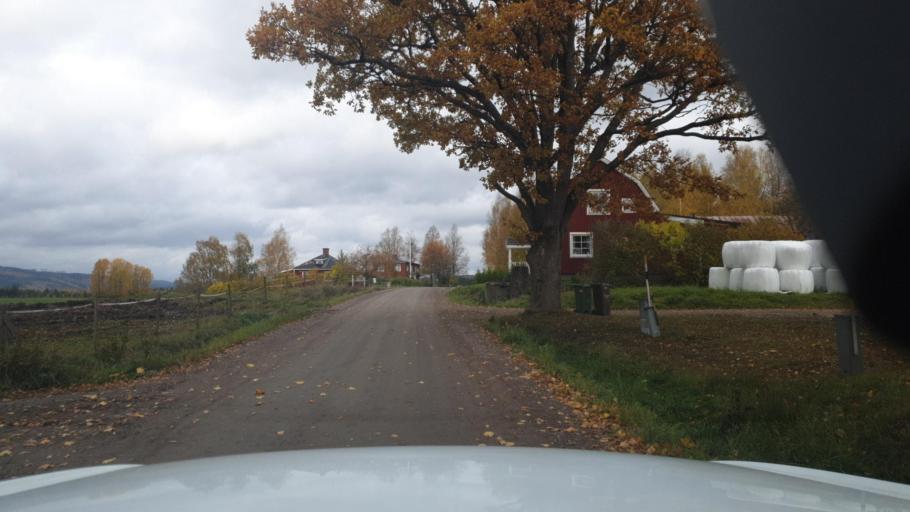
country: SE
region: Vaermland
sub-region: Sunne Kommun
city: Sunne
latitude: 59.7985
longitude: 13.1059
